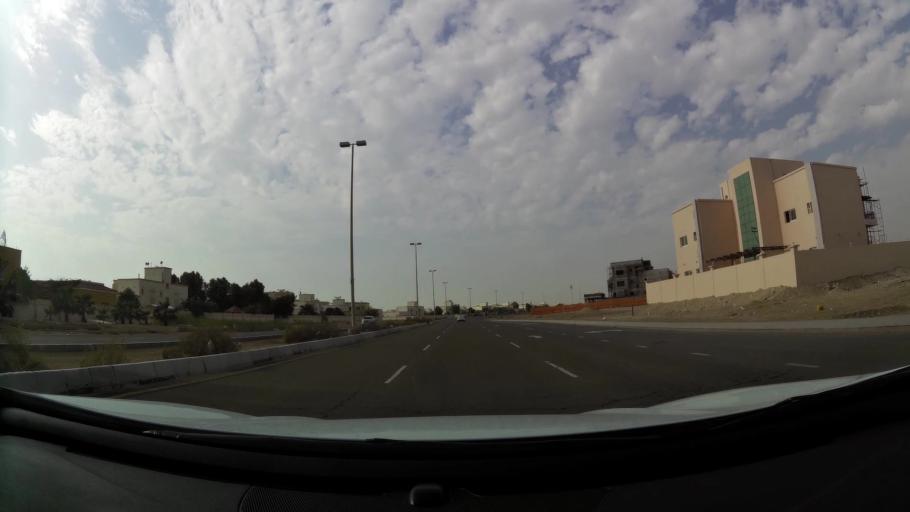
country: AE
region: Abu Dhabi
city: Abu Dhabi
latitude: 24.3430
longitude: 54.5674
